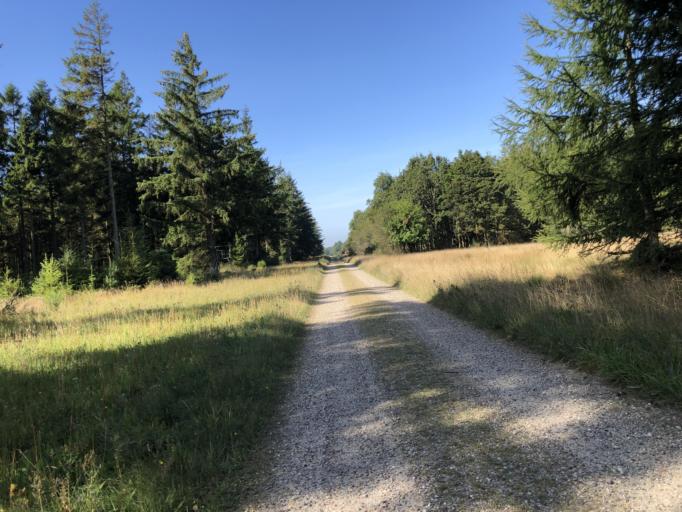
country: DK
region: Central Jutland
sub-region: Lemvig Kommune
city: Lemvig
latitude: 56.4772
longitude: 8.3241
